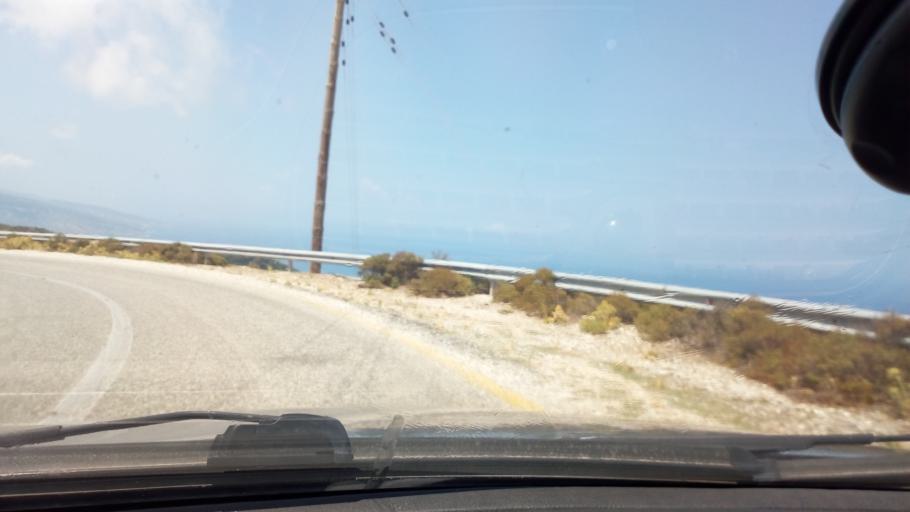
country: GR
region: North Aegean
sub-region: Nomos Samou
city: Agios Kirykos
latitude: 37.6508
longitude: 26.2816
